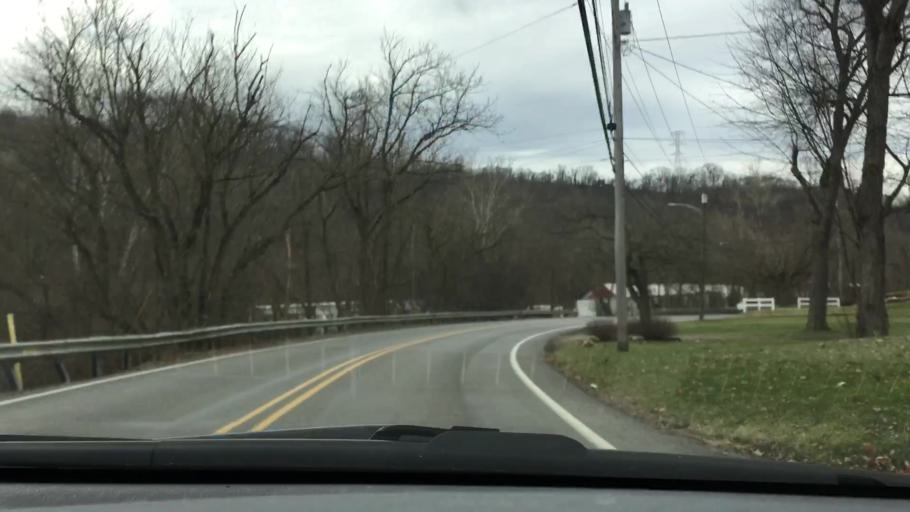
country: US
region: Pennsylvania
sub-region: Allegheny County
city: Sturgeon
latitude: 40.3759
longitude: -80.2169
